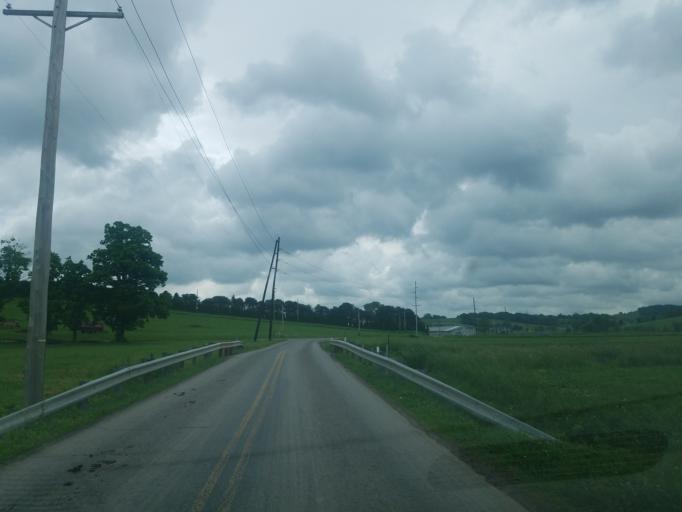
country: US
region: Ohio
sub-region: Tuscarawas County
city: Sugarcreek
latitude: 40.5318
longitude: -81.7273
